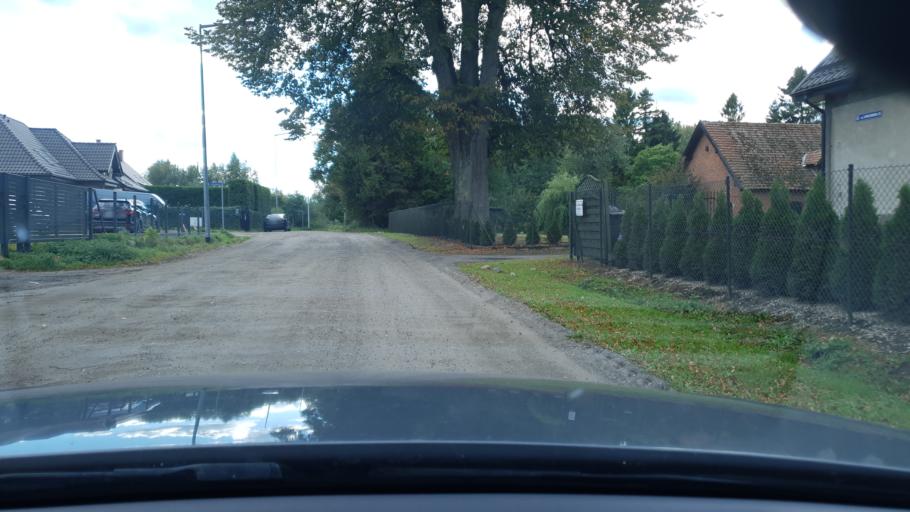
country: PL
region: Pomeranian Voivodeship
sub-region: Powiat wejherowski
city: Reda
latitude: 54.5800
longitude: 18.3123
